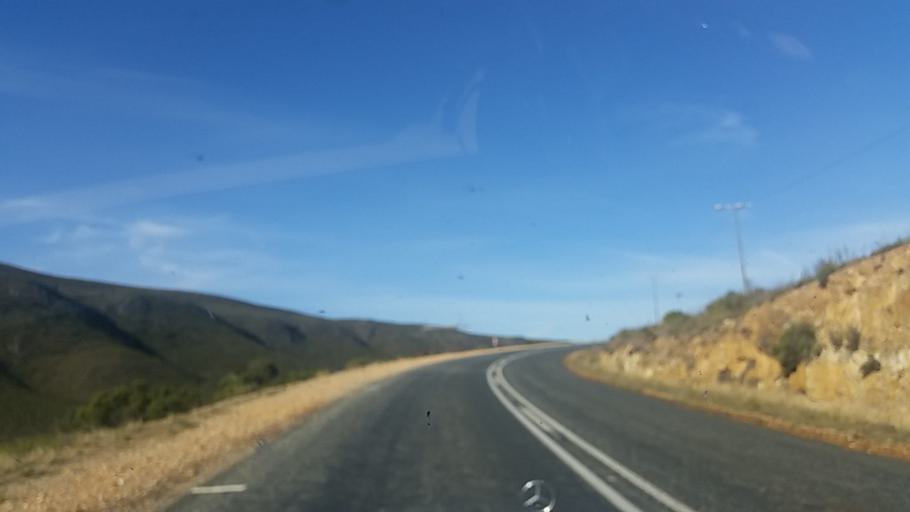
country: ZA
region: Western Cape
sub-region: Eden District Municipality
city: Knysna
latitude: -33.7424
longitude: 23.0011
